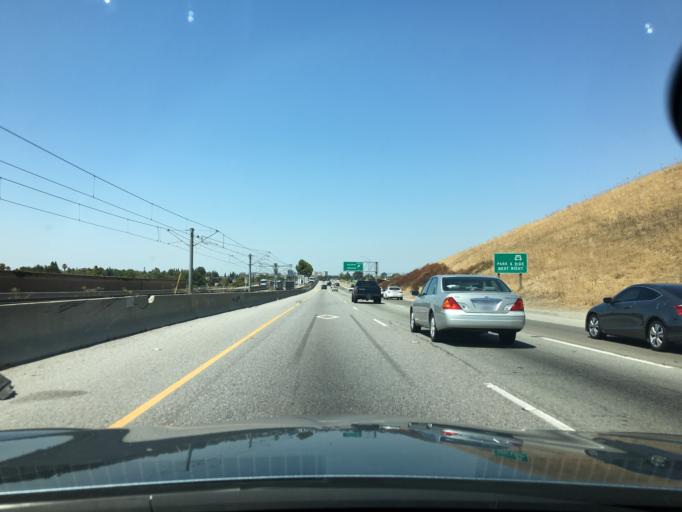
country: US
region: California
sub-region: Santa Clara County
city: Seven Trees
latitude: 37.2899
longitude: -121.8709
